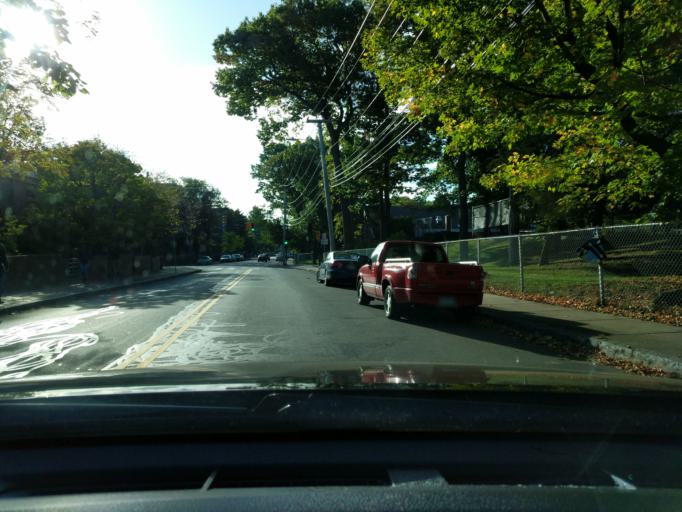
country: US
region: Massachusetts
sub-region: Middlesex County
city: Cambridge
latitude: 42.3825
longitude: -71.1272
